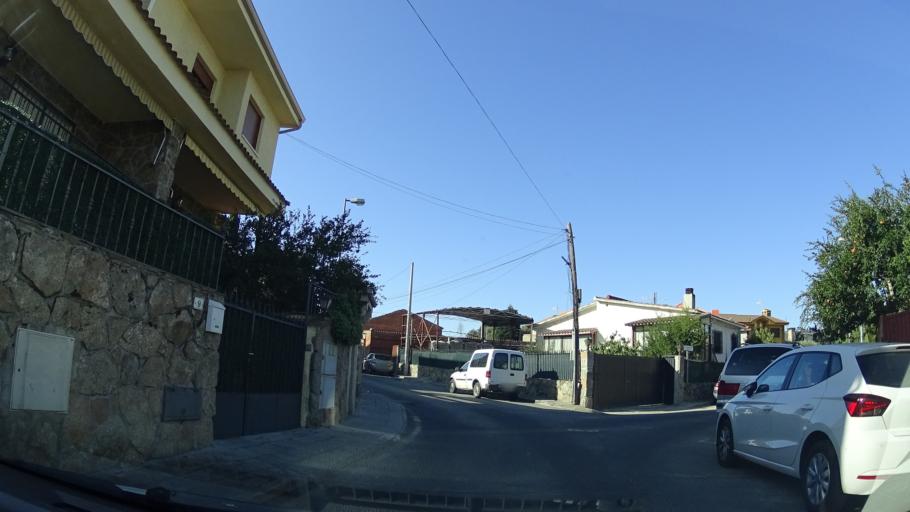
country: ES
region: Madrid
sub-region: Provincia de Madrid
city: Colmenarejo
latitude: 40.5595
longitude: -4.0191
